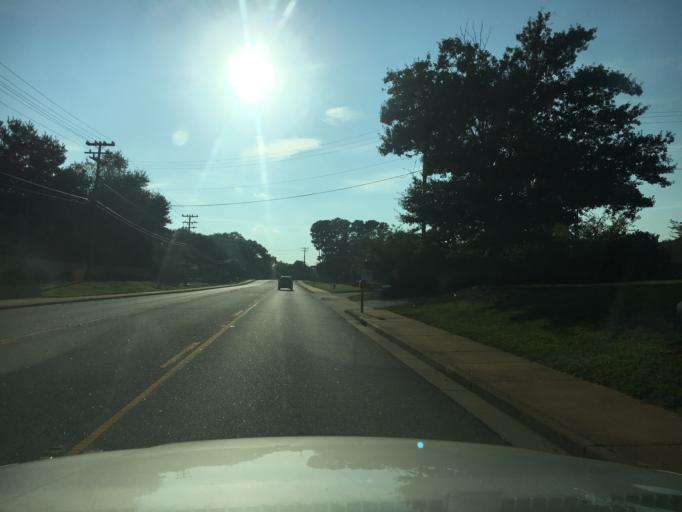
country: US
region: South Carolina
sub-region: Greenville County
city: Taylors
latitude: 34.8905
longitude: -82.2745
